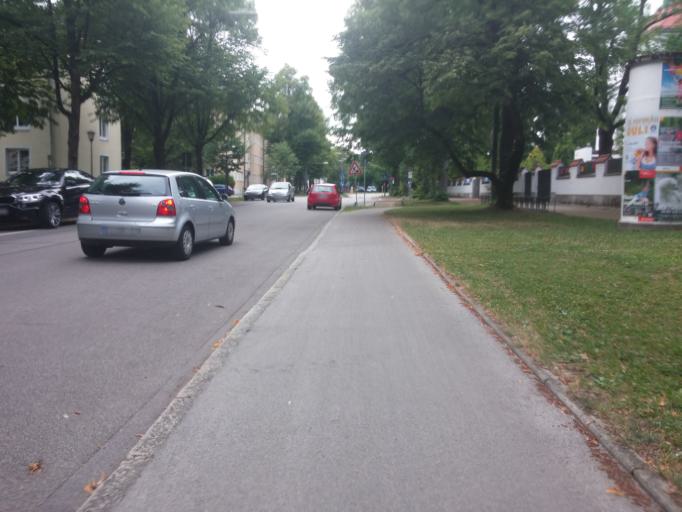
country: DE
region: Bavaria
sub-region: Upper Bavaria
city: Bogenhausen
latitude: 48.1499
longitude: 11.6112
